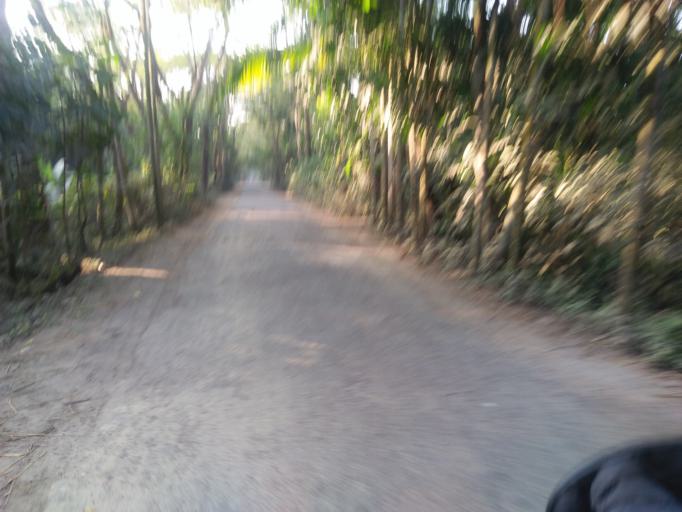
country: BD
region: Barisal
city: Bhola
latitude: 22.7532
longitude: 90.6297
